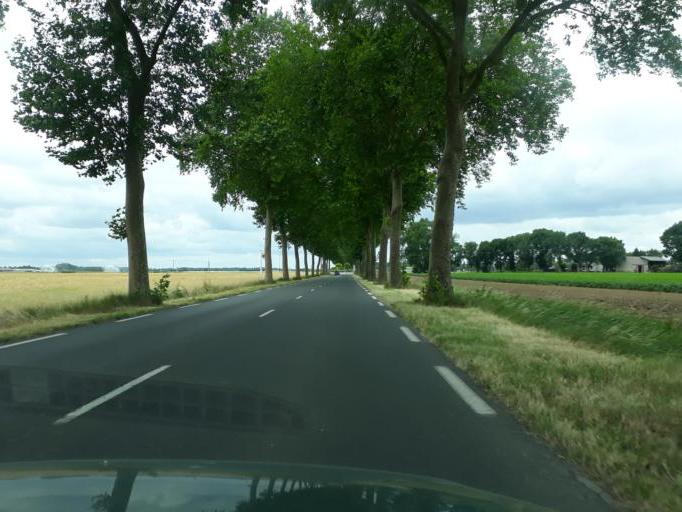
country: FR
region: Centre
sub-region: Departement du Loiret
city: Saint-Denis-en-Val
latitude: 47.8593
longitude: 1.9850
